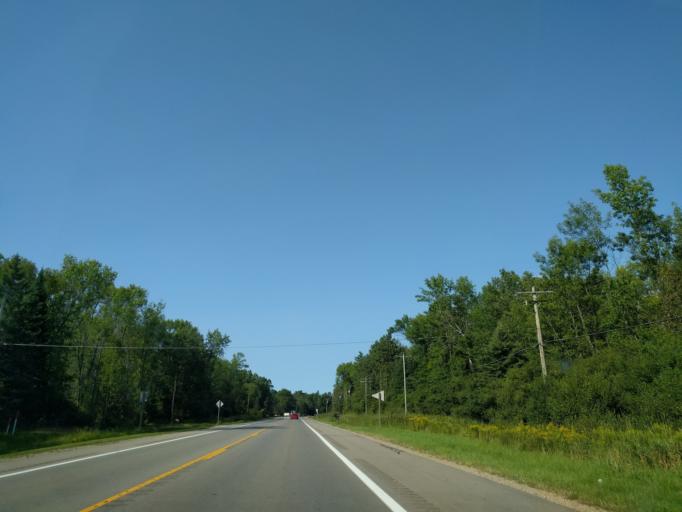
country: US
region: Michigan
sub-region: Menominee County
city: Menominee
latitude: 45.1595
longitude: -87.5908
